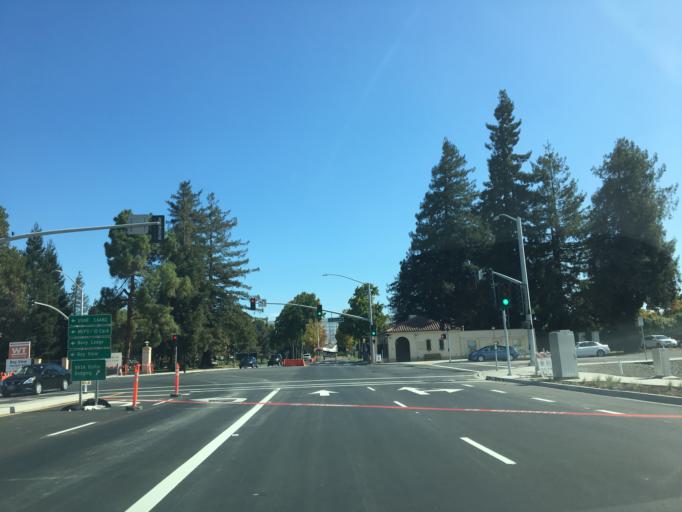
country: US
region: California
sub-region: Santa Clara County
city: Mountain View
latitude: 37.4096
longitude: -122.0641
